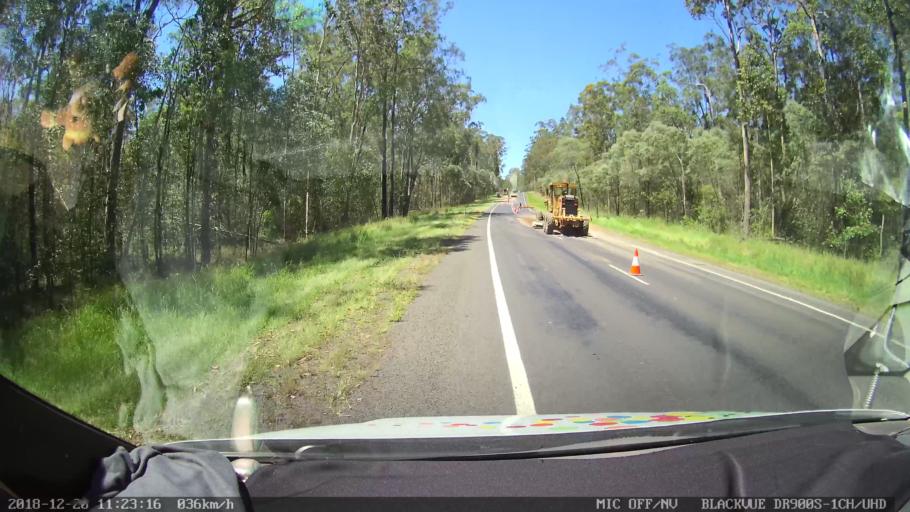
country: AU
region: New South Wales
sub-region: Richmond Valley
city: Casino
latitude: -29.0647
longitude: 153.0046
